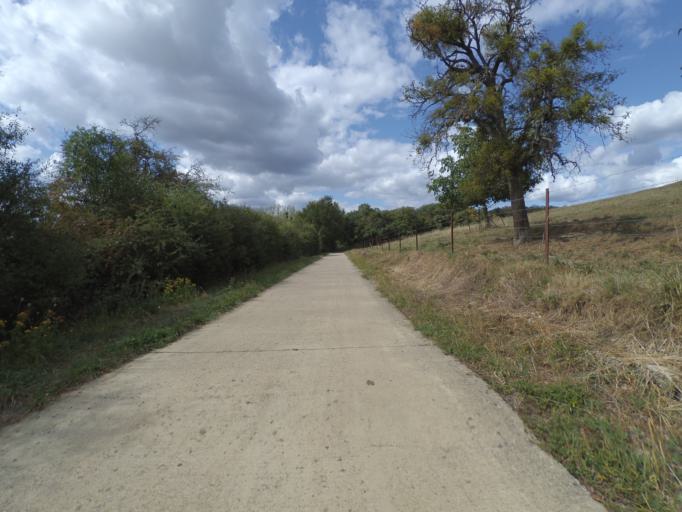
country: LU
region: Grevenmacher
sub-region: Canton de Remich
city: Mondorf-les-Bains
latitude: 49.5202
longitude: 6.3116
